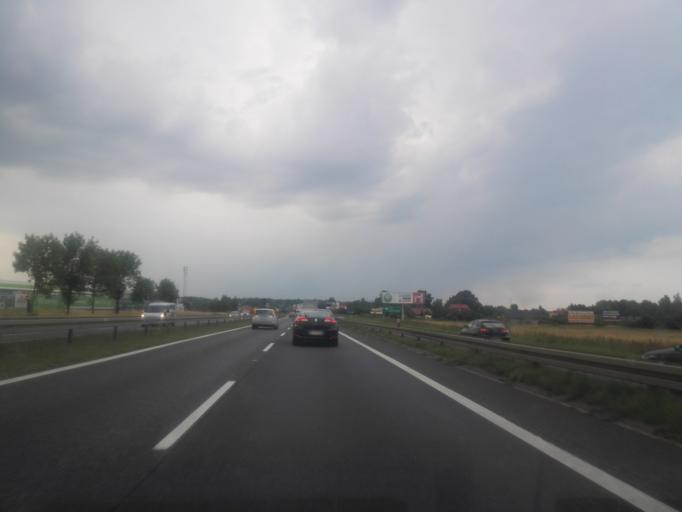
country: PL
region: Silesian Voivodeship
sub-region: Powiat czestochowski
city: Huta Stara B
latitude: 50.7309
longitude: 19.1616
